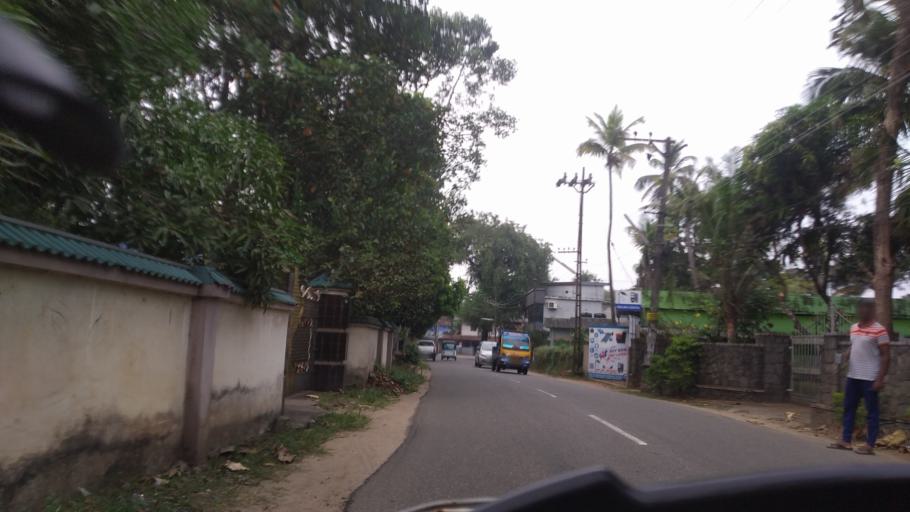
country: IN
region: Kerala
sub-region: Thrissur District
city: Kodungallur
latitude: 10.1474
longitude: 76.2456
